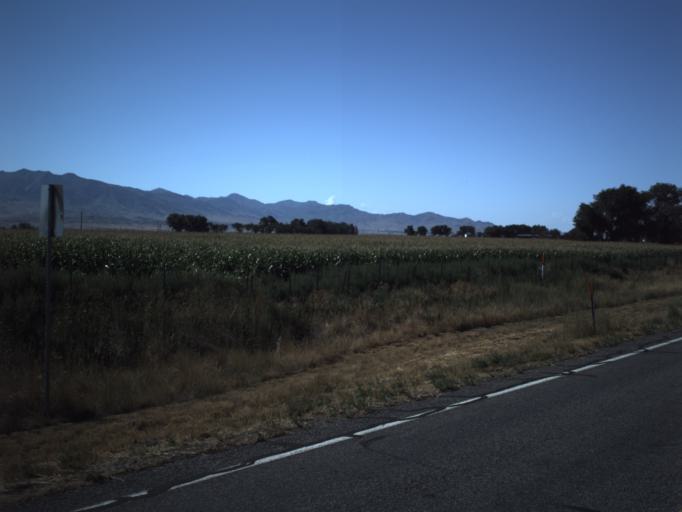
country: US
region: Utah
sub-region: Millard County
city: Delta
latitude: 39.5278
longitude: -112.3714
